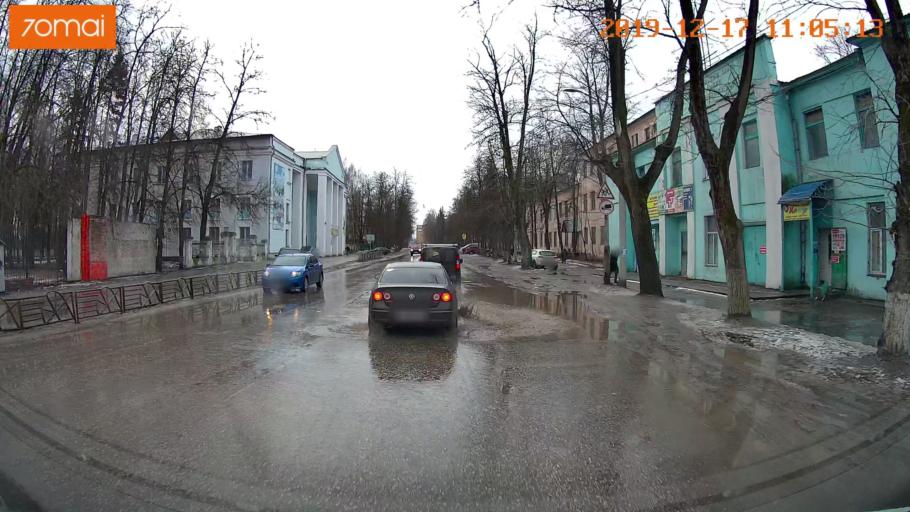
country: RU
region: Vladimir
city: Gus'-Khrustal'nyy
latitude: 55.6221
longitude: 40.6433
